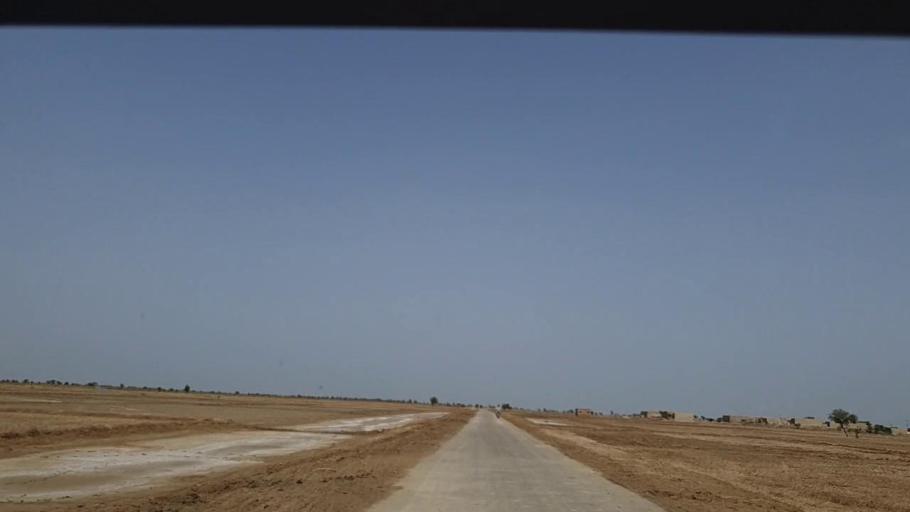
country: PK
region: Sindh
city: Johi
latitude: 26.7707
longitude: 67.6433
